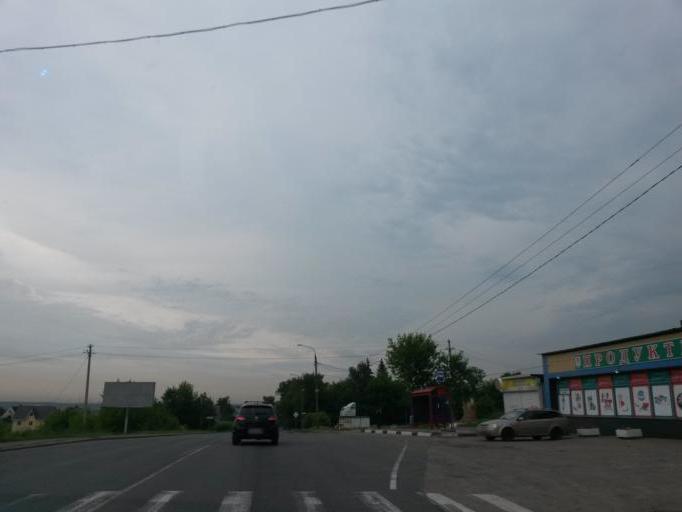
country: RU
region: Moskovskaya
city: Yam
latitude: 55.4623
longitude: 37.7016
